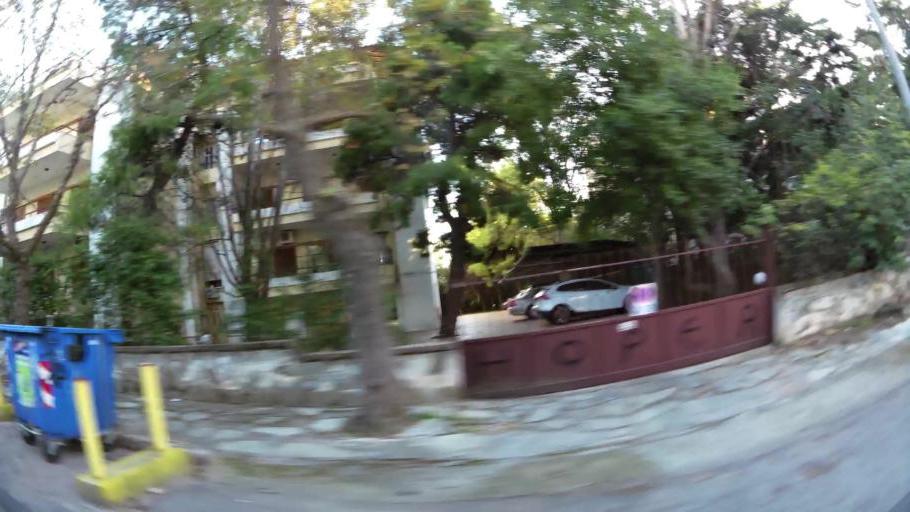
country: GR
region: Attica
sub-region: Nomarchia Athinas
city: Nea Erythraia
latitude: 38.0866
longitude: 23.8208
